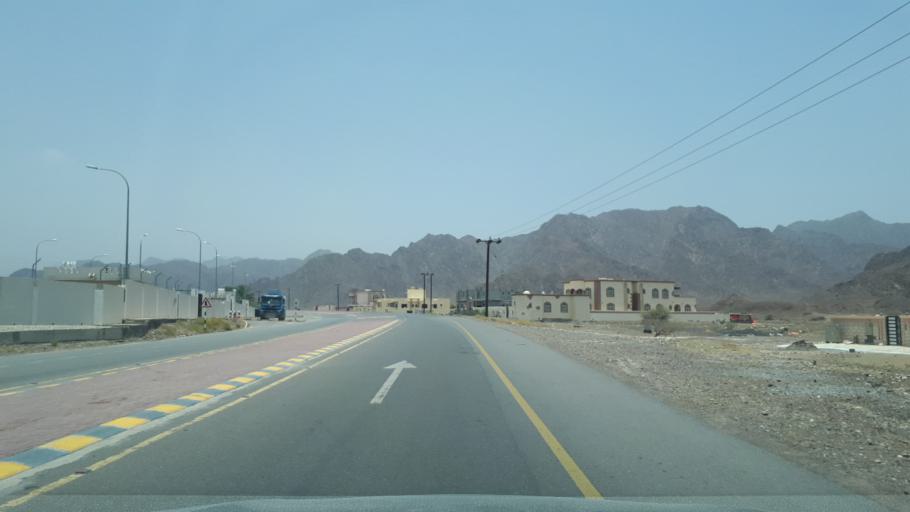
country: OM
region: Al Batinah
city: Rustaq
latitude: 23.4303
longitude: 57.2794
